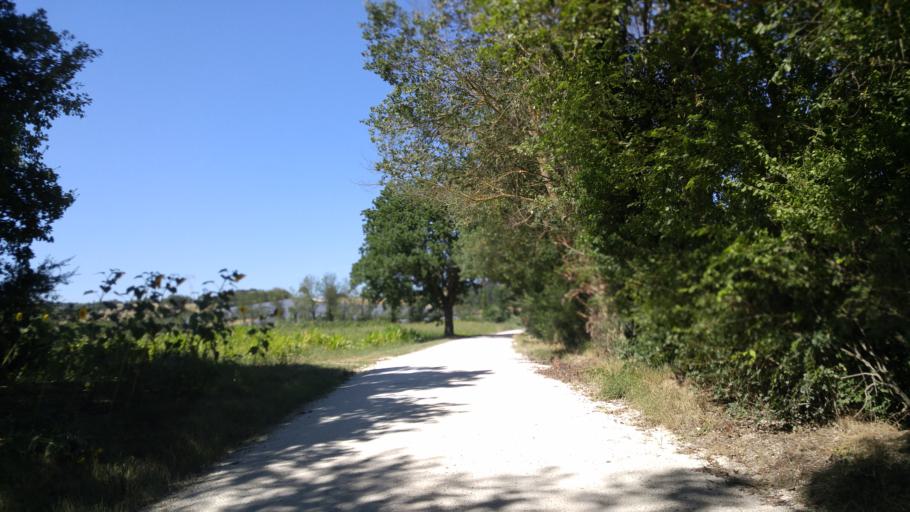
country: IT
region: The Marches
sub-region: Provincia di Pesaro e Urbino
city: Mombaroccio
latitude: 43.8160
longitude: 12.8818
